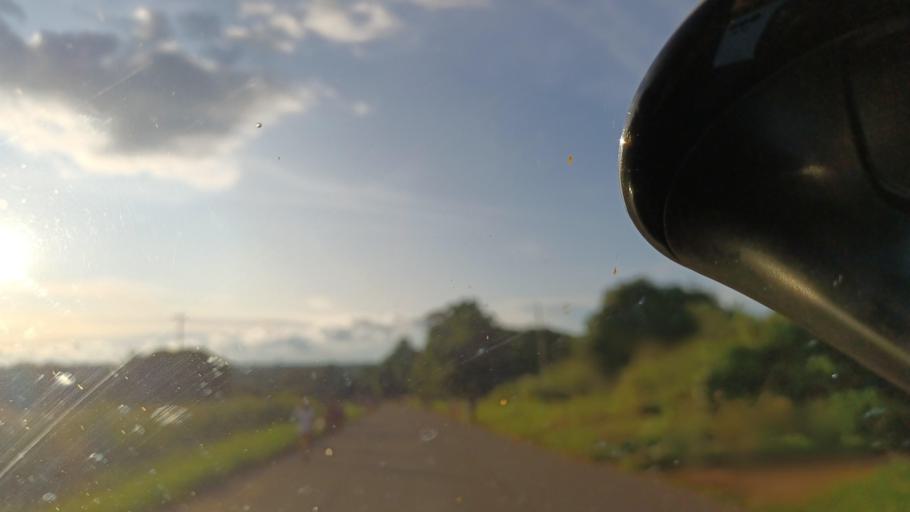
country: ZM
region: North-Western
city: Kasempa
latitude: -13.4595
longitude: 25.8491
